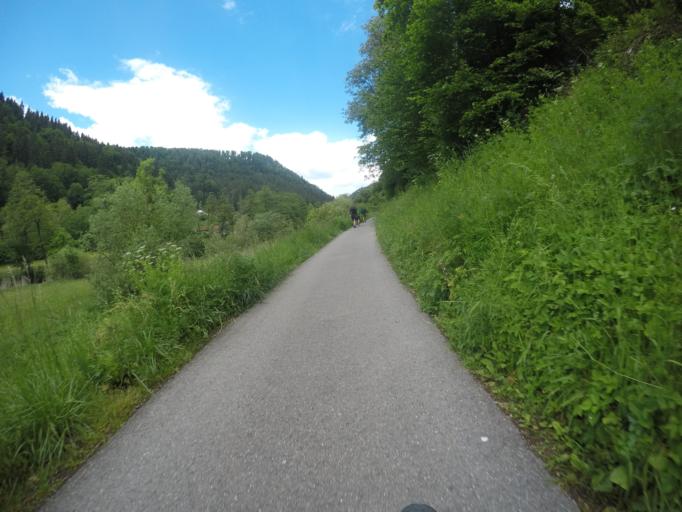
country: DE
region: Baden-Wuerttemberg
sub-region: Karlsruhe Region
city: Bad Liebenzell
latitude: 48.7460
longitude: 8.7320
